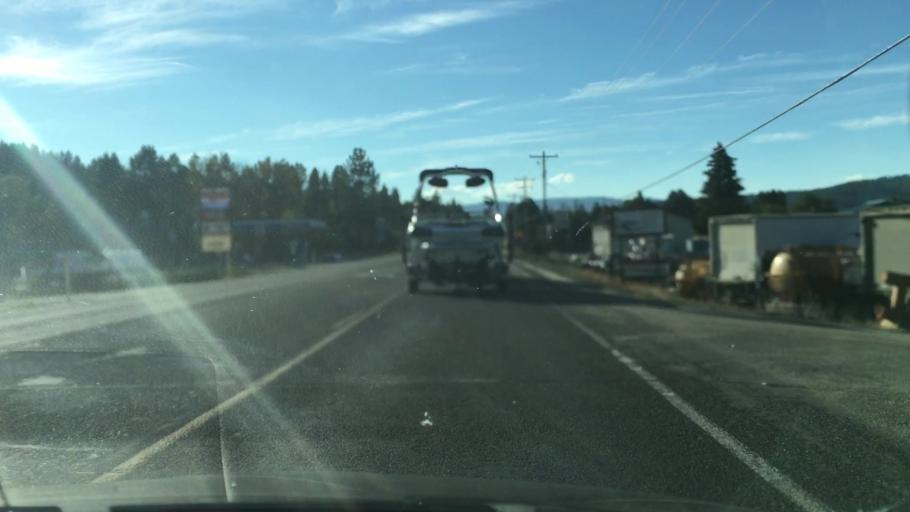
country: US
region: Idaho
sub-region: Valley County
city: Cascade
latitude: 44.5043
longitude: -116.0283
